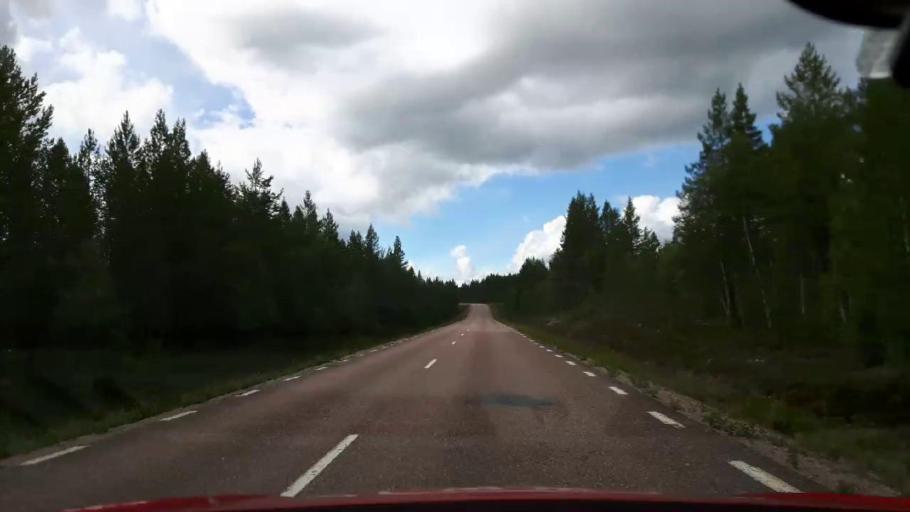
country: SE
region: Jaemtland
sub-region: Harjedalens Kommun
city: Sveg
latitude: 61.8304
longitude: 13.8859
